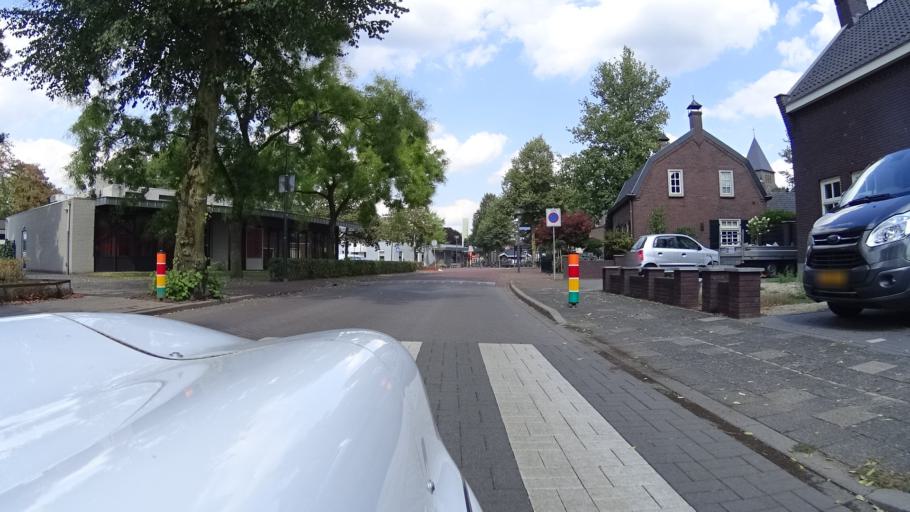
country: NL
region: North Brabant
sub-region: Gemeente Uden
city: Volkel
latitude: 51.6430
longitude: 5.6539
